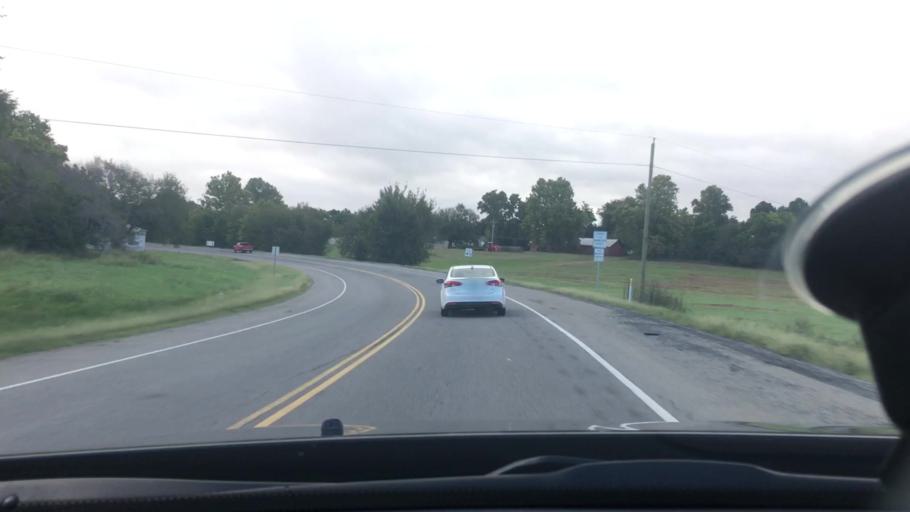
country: US
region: Oklahoma
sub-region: Coal County
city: Coalgate
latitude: 34.5433
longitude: -96.2283
